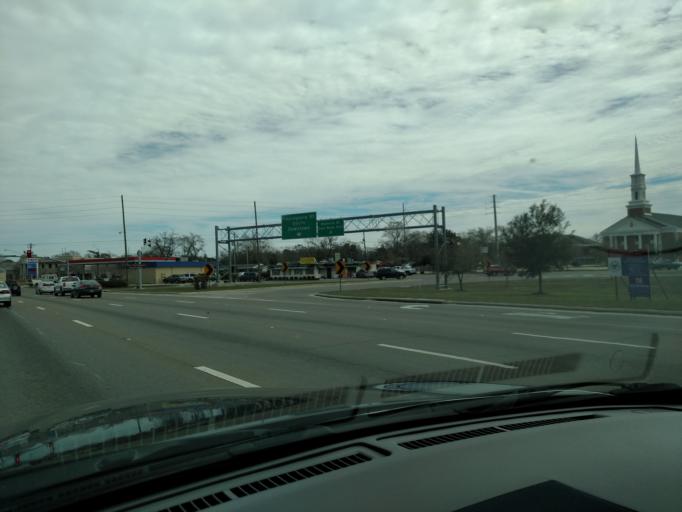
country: US
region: Mississippi
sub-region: Jackson County
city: Pascagoula
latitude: 30.3710
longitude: -88.5556
